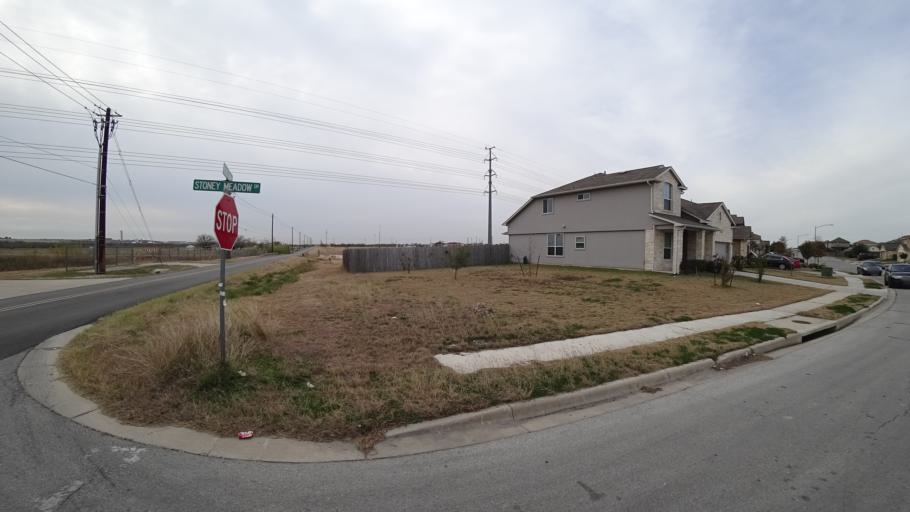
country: US
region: Texas
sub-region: Travis County
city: Garfield
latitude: 30.1589
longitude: -97.6367
